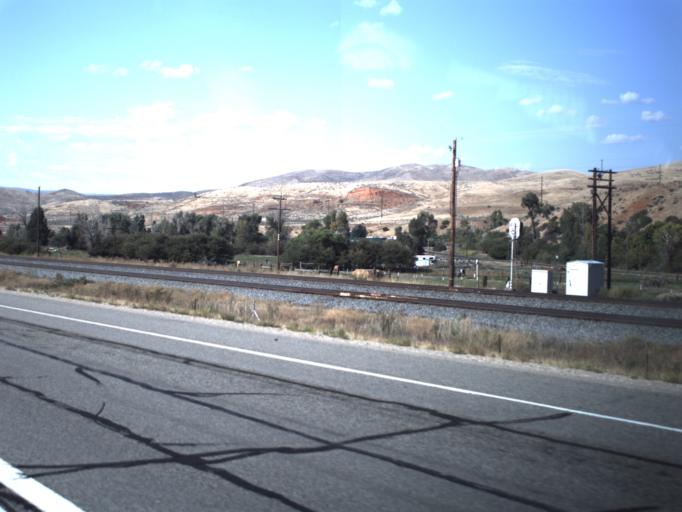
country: US
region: Utah
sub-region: Summit County
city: Coalville
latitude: 41.0206
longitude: -111.4930
